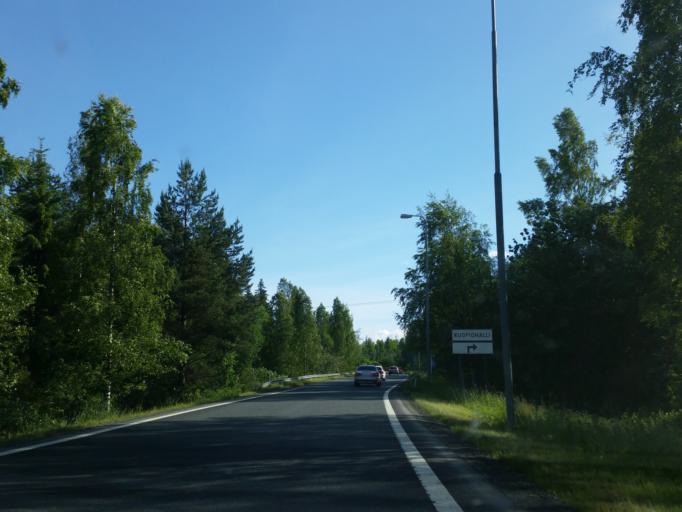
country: FI
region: Northern Savo
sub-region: Kuopio
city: Kuopio
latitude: 62.9080
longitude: 27.6865
